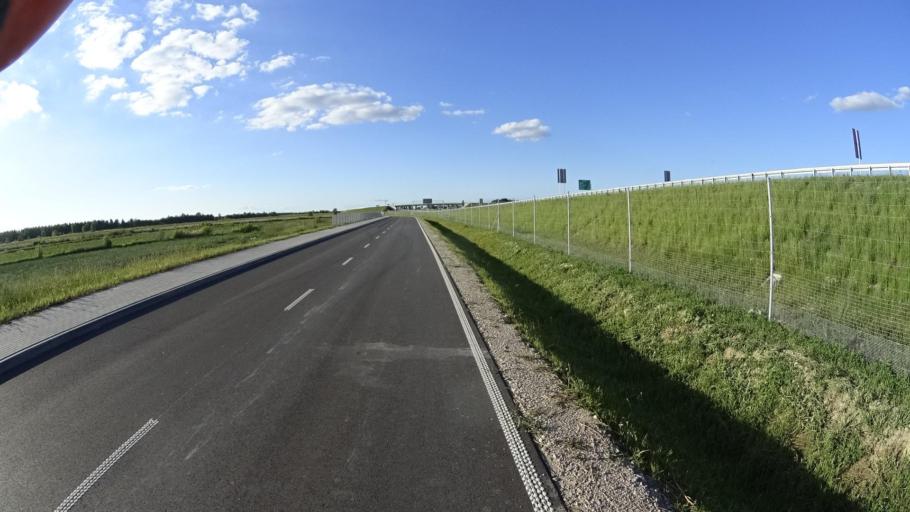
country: PL
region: Masovian Voivodeship
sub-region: Powiat piaseczynski
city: Lesznowola
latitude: 52.0969
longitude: 20.9707
